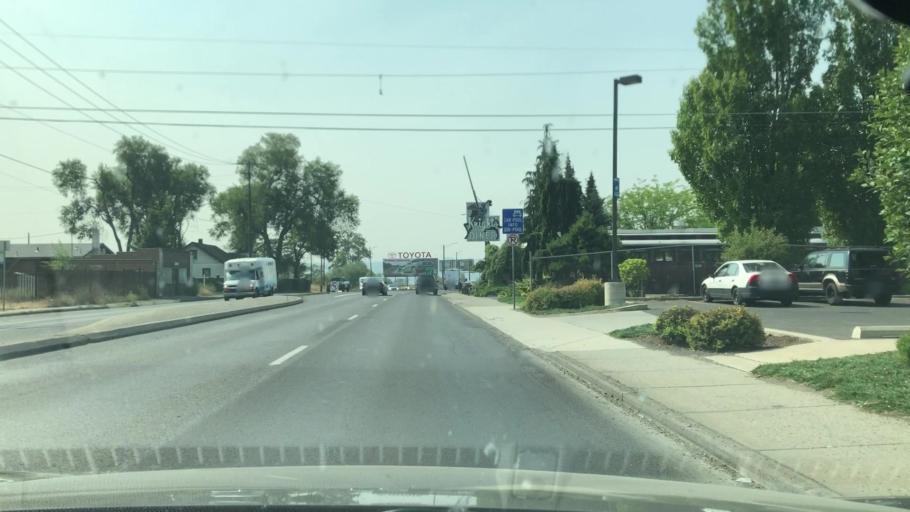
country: US
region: Washington
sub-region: Spokane County
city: Spokane
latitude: 47.6849
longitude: -117.3652
